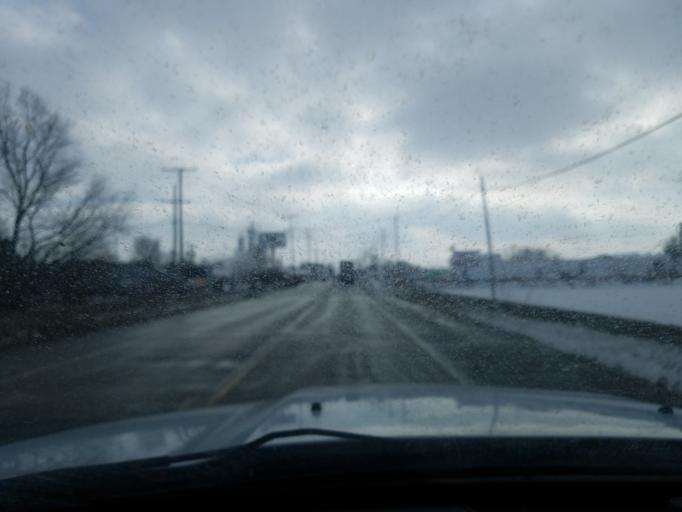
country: US
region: Indiana
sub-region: Marshall County
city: Bremen
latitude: 41.4532
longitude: -86.1562
